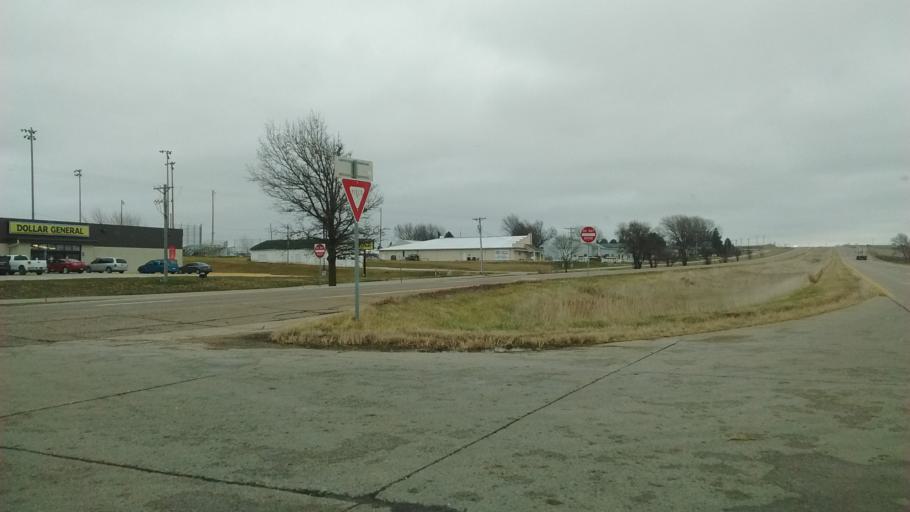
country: US
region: Iowa
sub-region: Woodbury County
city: Moville
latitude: 42.4817
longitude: -96.0654
